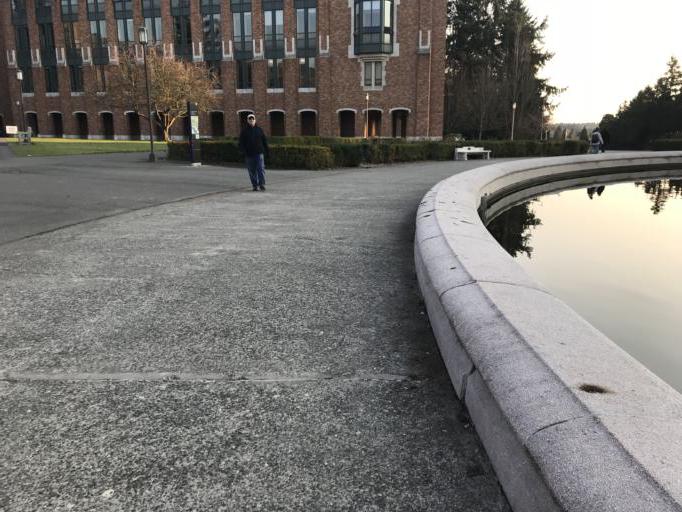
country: US
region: Washington
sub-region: King County
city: Seattle
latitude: 47.6542
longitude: -122.3076
